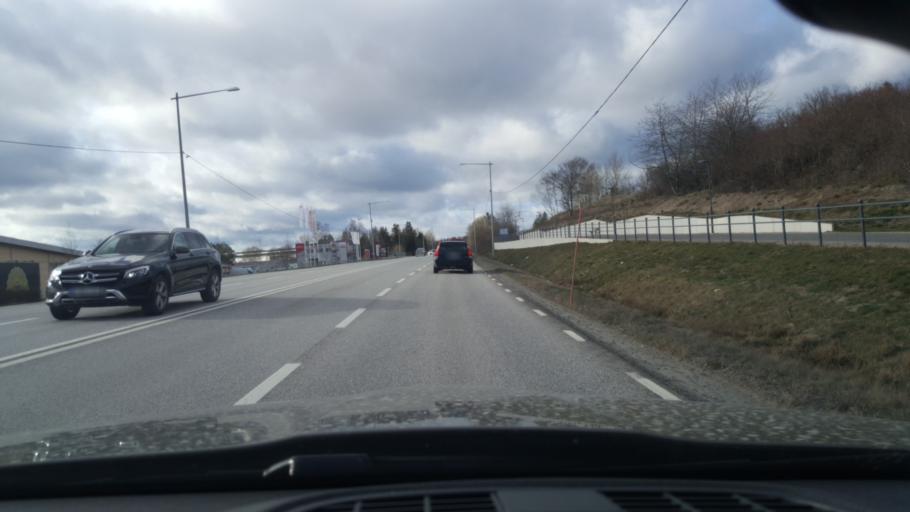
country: SE
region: Stockholm
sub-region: Osterakers Kommun
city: Akersberga
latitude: 59.4824
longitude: 18.2831
